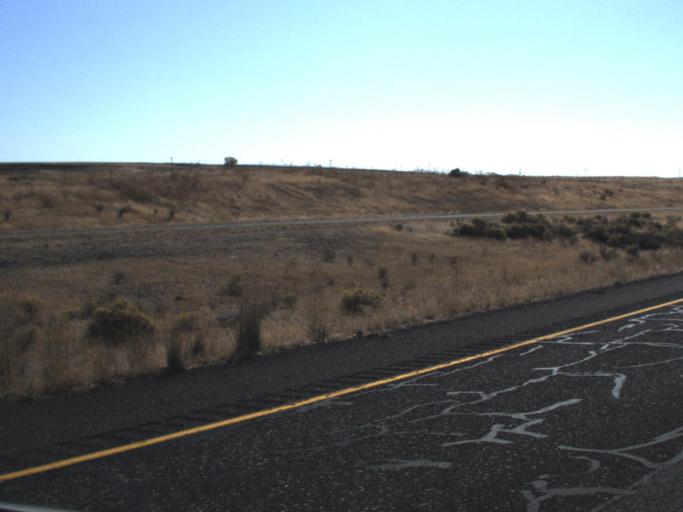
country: US
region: Washington
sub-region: Franklin County
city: Basin City
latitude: 46.5298
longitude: -119.0153
